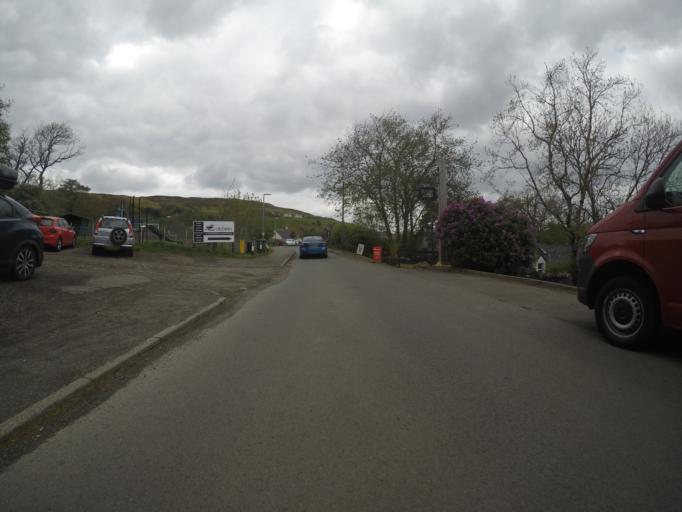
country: GB
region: Scotland
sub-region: Highland
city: Isle of Skye
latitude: 57.3015
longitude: -6.3528
